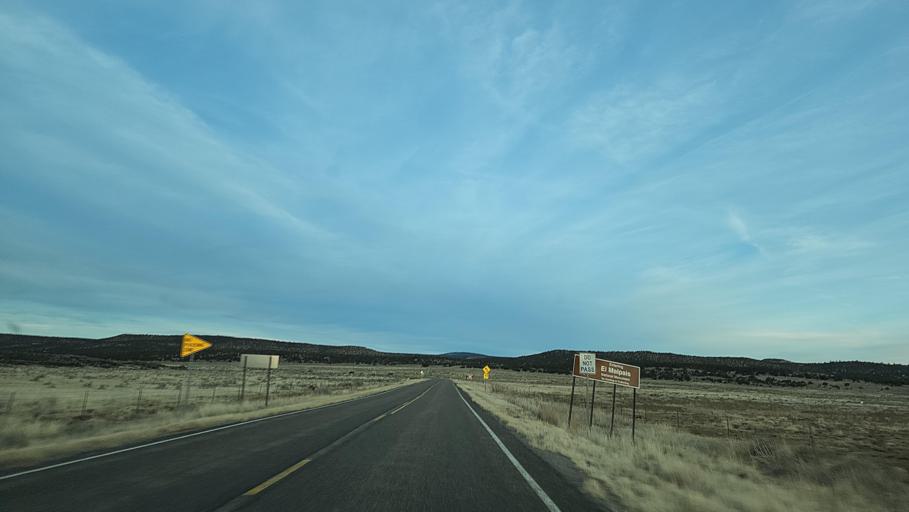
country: US
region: New Mexico
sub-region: Cibola County
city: Grants
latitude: 34.7100
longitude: -107.9940
